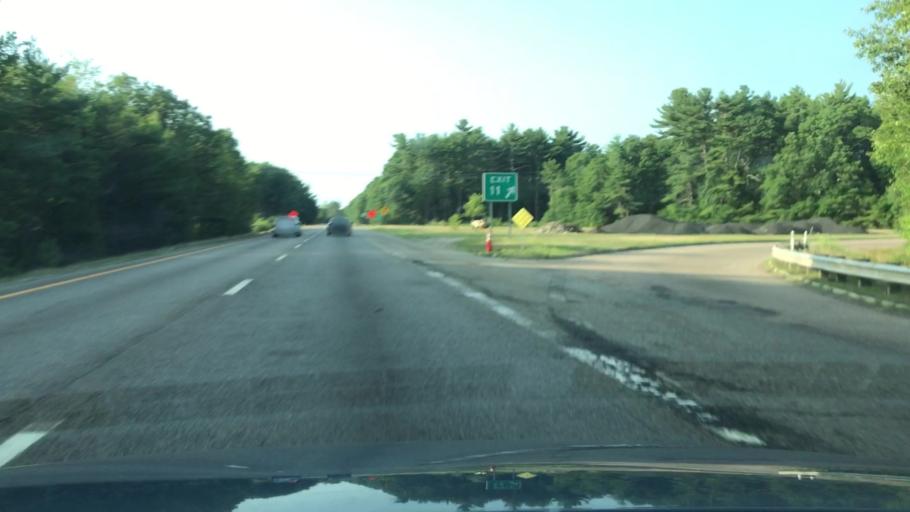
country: US
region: Massachusetts
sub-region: Plymouth County
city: Marshfield
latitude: 42.0549
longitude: -70.7254
